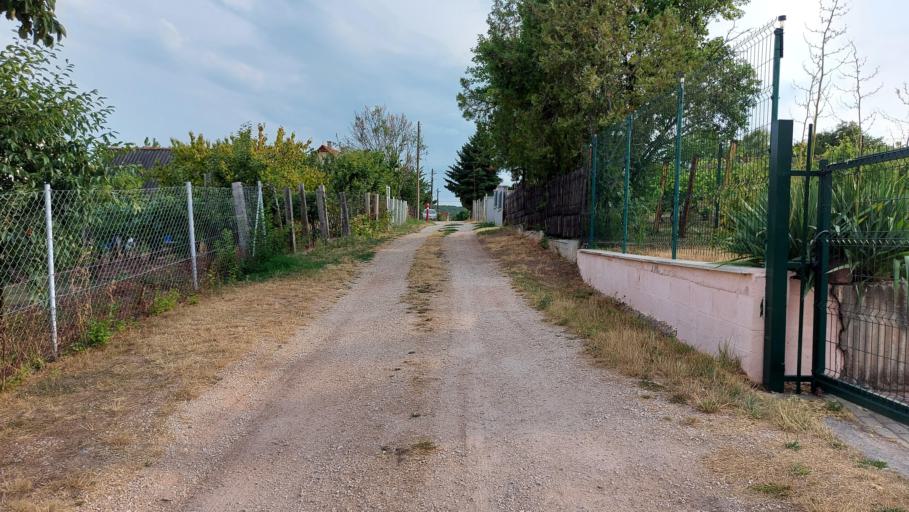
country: HU
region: Veszprem
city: Balatonalmadi
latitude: 47.0447
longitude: 18.0014
